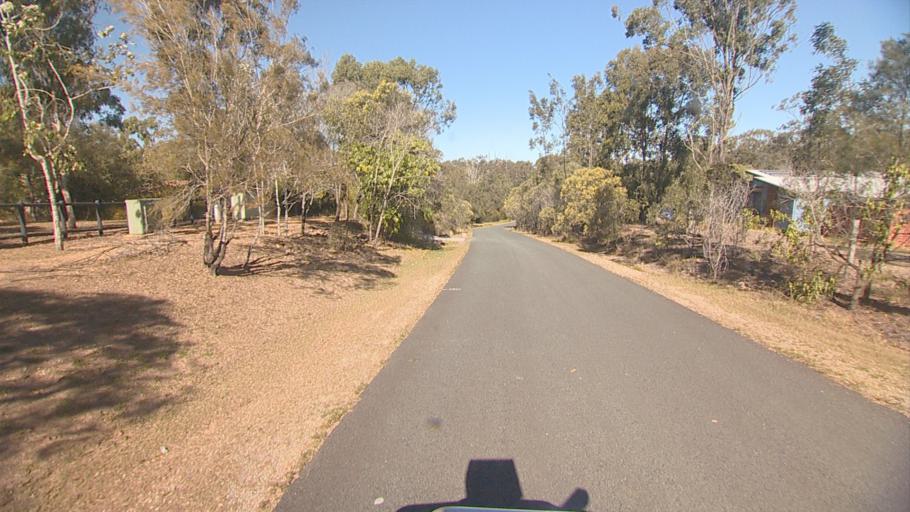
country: AU
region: Queensland
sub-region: Ipswich
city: Springfield Lakes
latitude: -27.7122
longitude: 152.9322
